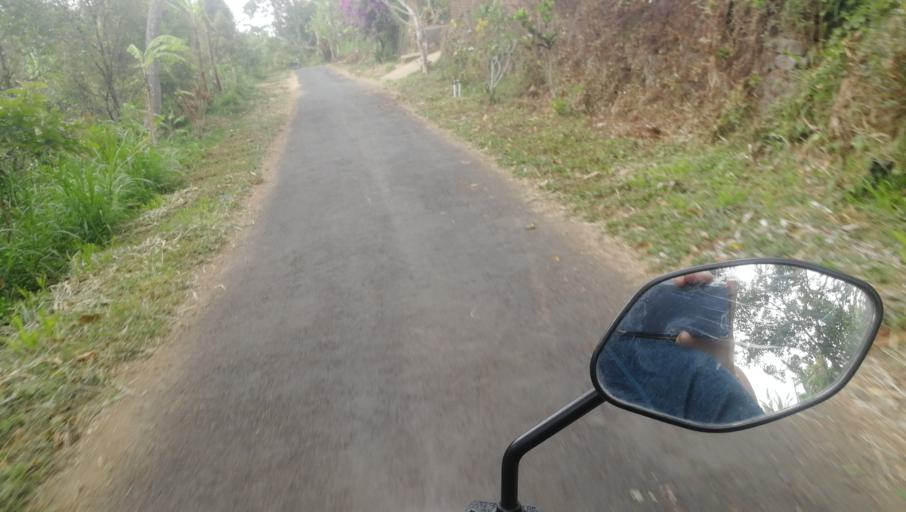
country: ID
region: Bali
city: Banjar Ambengan
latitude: -8.2195
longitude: 115.1102
